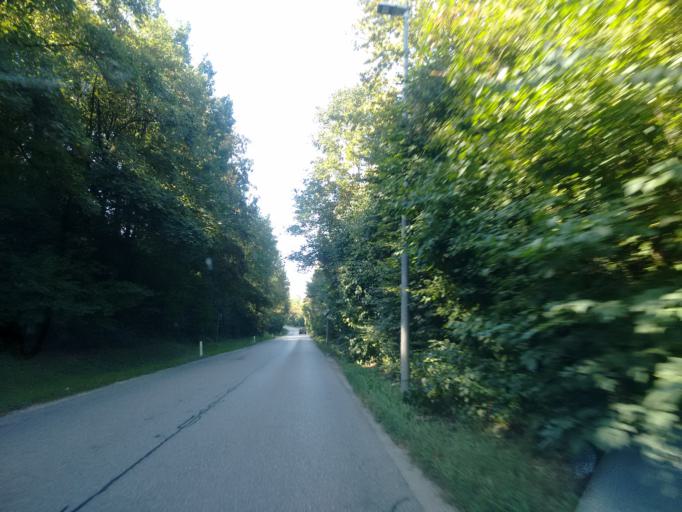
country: AT
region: Upper Austria
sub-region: Wels Stadt
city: Wels
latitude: 48.1610
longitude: 13.9920
